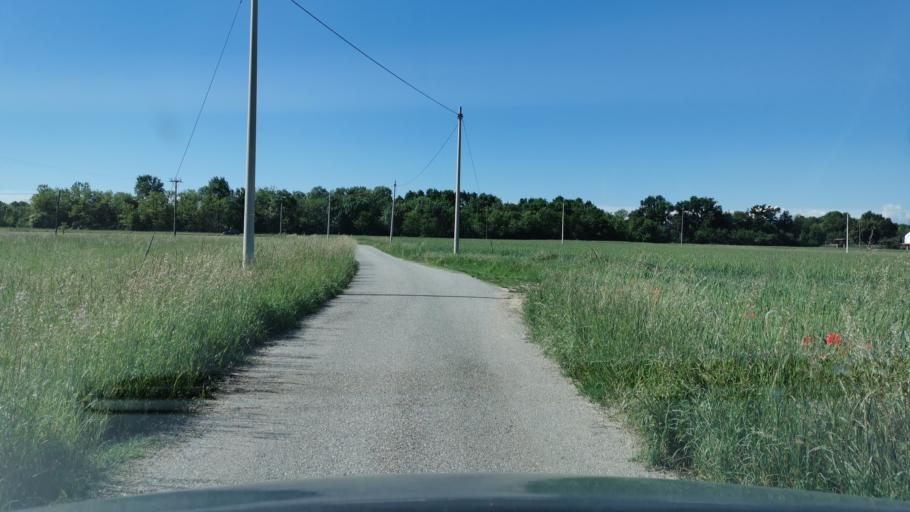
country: IT
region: Piedmont
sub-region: Provincia di Torino
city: Volpiano
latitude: 45.2000
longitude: 7.7460
